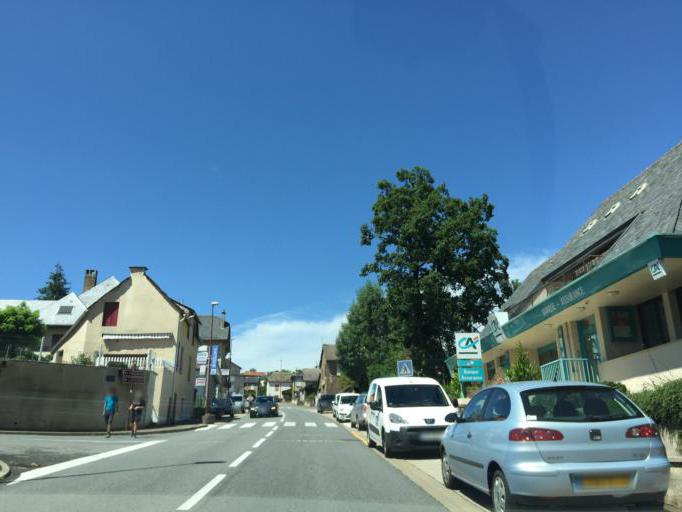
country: FR
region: Midi-Pyrenees
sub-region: Departement de l'Aveyron
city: Pont-de-Salars
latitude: 44.2818
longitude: 2.7277
